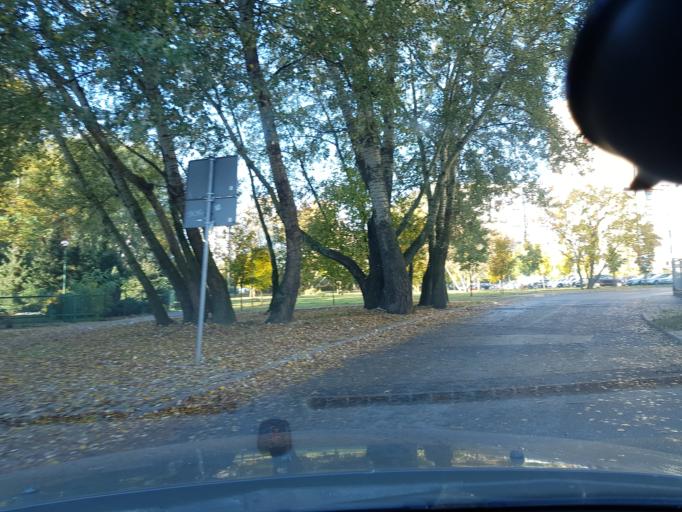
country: PL
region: Masovian Voivodeship
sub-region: Warszawa
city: Bielany
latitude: 52.2827
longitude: 20.9370
